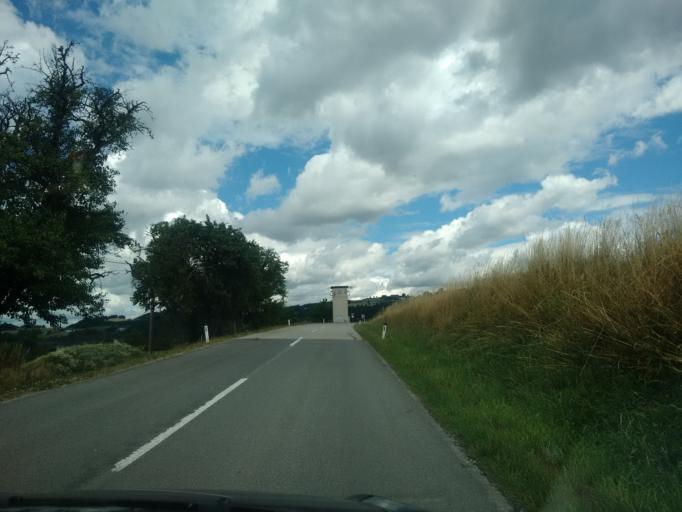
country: AT
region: Upper Austria
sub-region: Politischer Bezirk Urfahr-Umgebung
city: Walding
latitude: 48.3634
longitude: 14.1595
